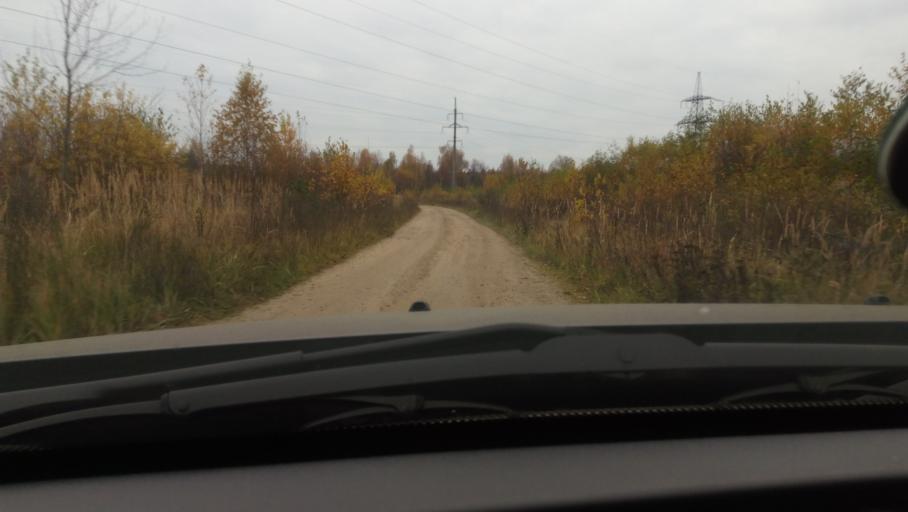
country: RU
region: Moskovskaya
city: Avsyunino
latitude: 55.5819
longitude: 39.2504
